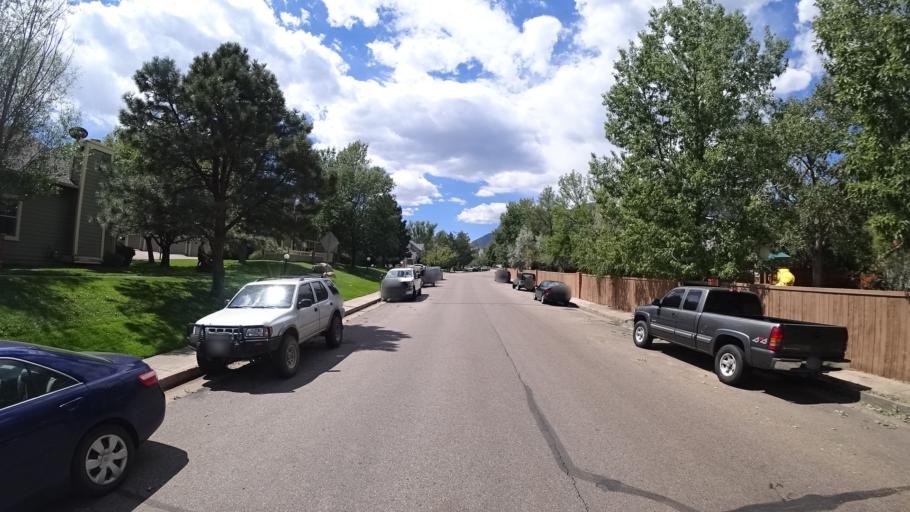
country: US
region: Colorado
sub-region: El Paso County
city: Stratmoor
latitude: 38.7722
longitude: -104.8151
